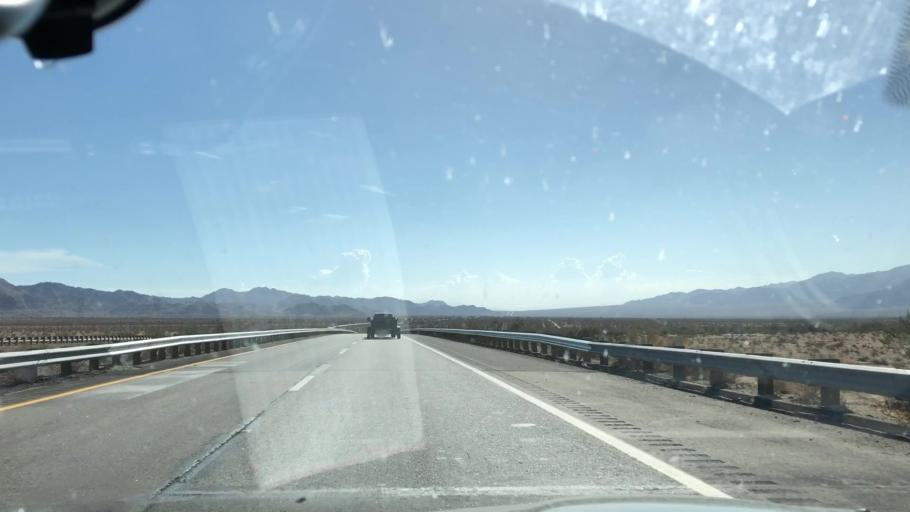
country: US
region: California
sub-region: Imperial County
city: Niland
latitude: 33.6764
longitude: -115.5698
